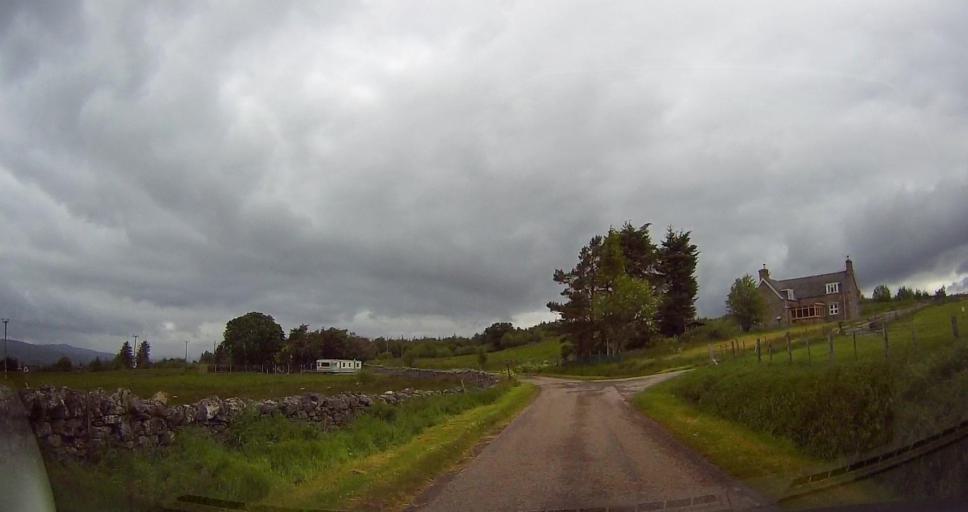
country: GB
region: Scotland
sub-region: Highland
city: Alness
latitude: 58.0795
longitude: -4.4468
